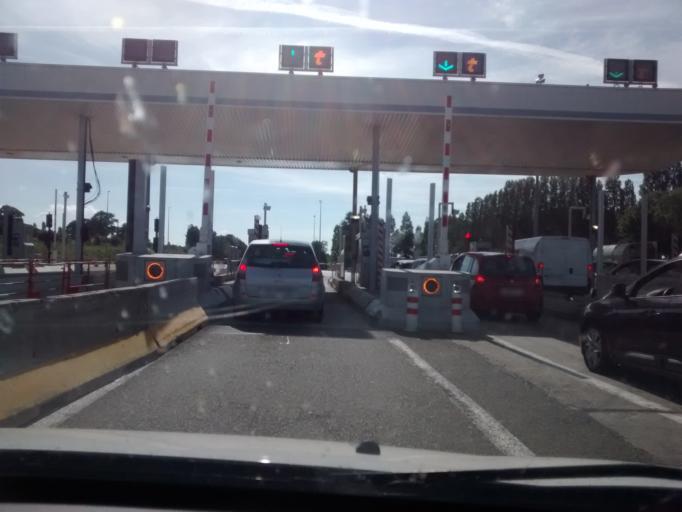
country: FR
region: Pays de la Loire
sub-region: Departement de la Mayenne
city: Saint-Pierre-la-Cour
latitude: 48.0832
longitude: -1.0272
